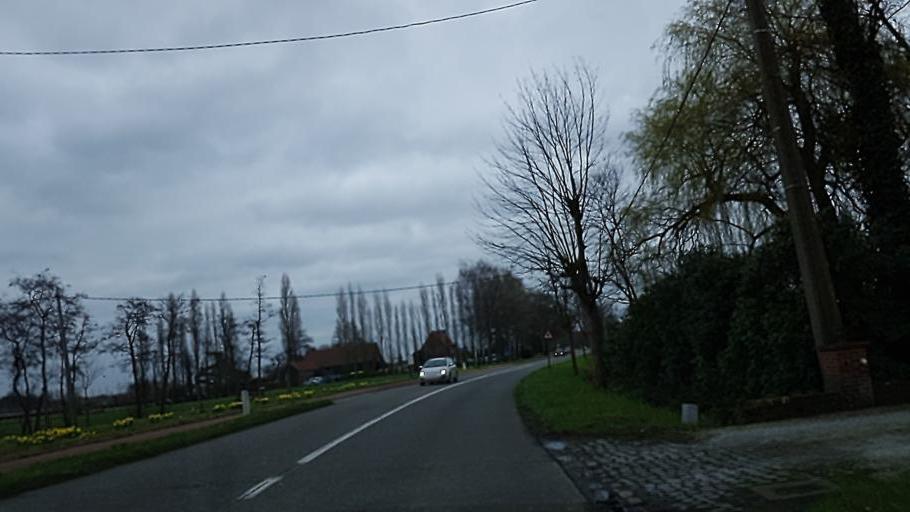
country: BE
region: Flanders
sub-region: Provincie Antwerpen
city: Lint
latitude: 51.1288
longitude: 4.5209
